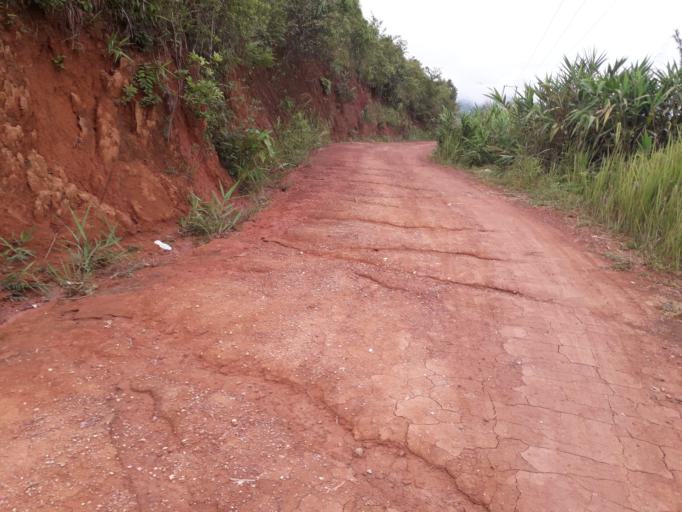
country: CN
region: Yunnan
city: Menglie
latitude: 22.2645
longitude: 101.5790
